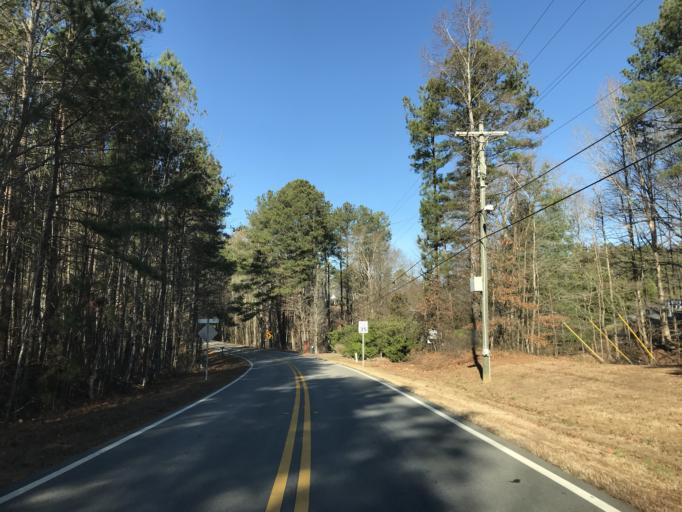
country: US
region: Georgia
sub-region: Paulding County
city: Dallas
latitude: 33.9819
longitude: -84.8836
